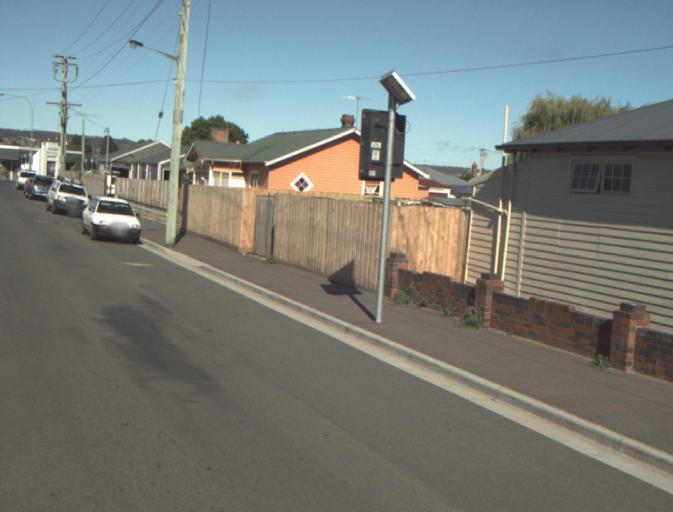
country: AU
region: Tasmania
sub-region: Launceston
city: Newnham
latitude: -41.4034
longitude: 147.1330
